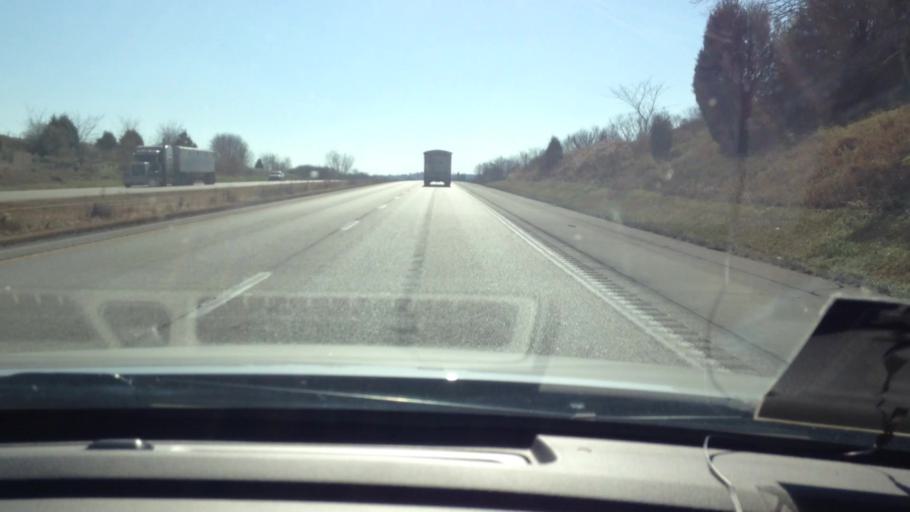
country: US
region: Missouri
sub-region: Platte County
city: Platte City
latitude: 39.4056
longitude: -94.7898
